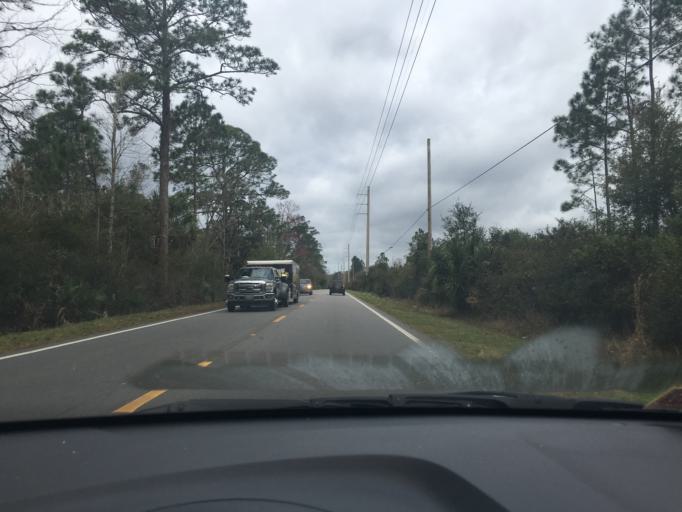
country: US
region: Florida
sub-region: Saint Johns County
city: Villano Beach
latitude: 30.0046
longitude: -81.4102
